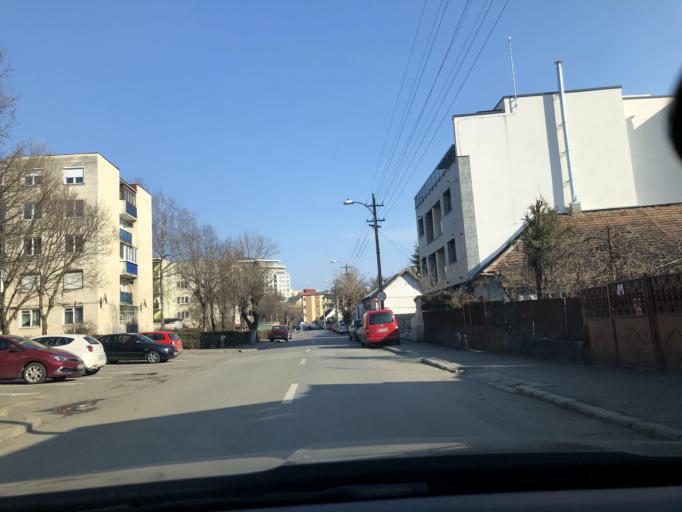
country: RO
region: Cluj
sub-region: Municipiul Cluj-Napoca
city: Cluj-Napoca
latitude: 46.7633
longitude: 23.5669
